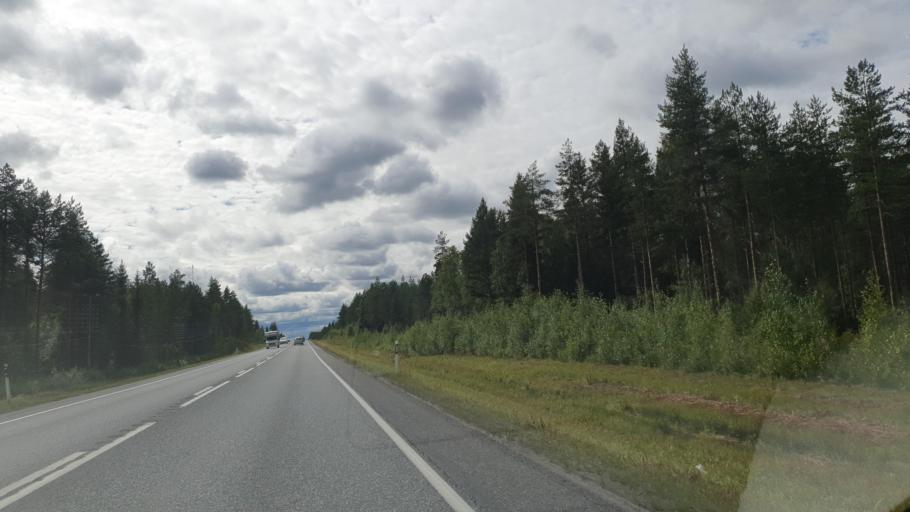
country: FI
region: Kainuu
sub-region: Kajaani
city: Kajaani
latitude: 64.1754
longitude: 27.5616
